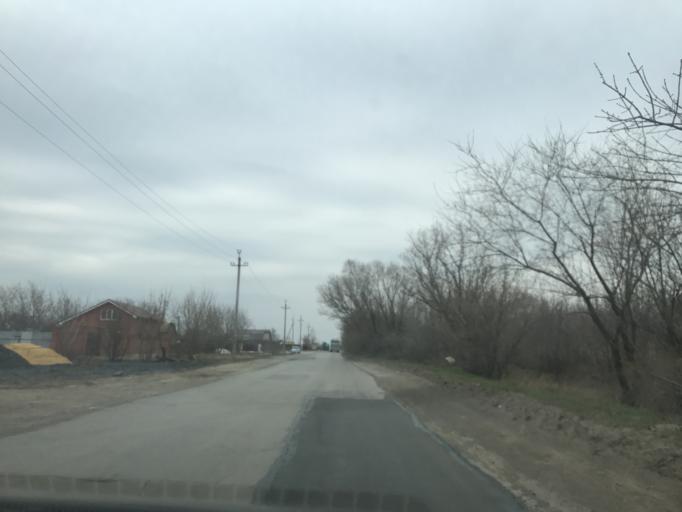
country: RU
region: Rostov
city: Novocherkassk
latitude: 47.3907
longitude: 40.0567
